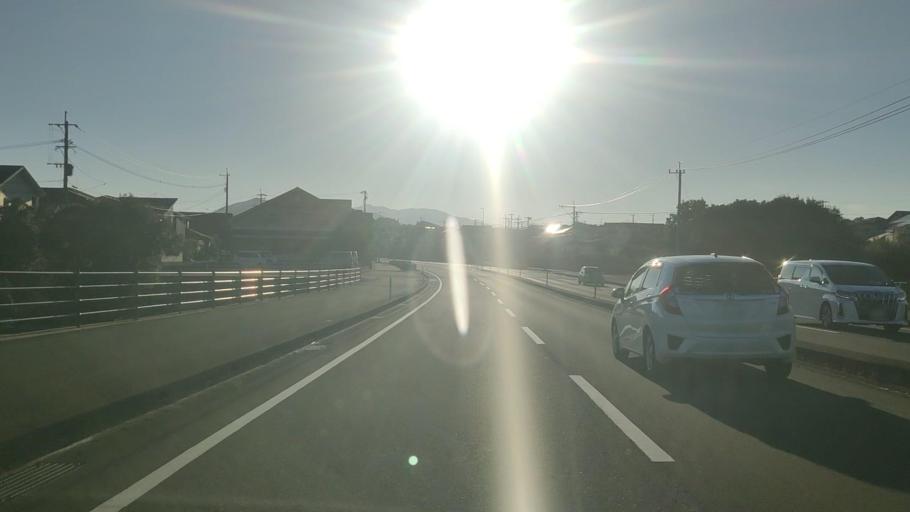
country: JP
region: Miyazaki
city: Miyazaki-shi
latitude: 31.8817
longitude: 131.3952
